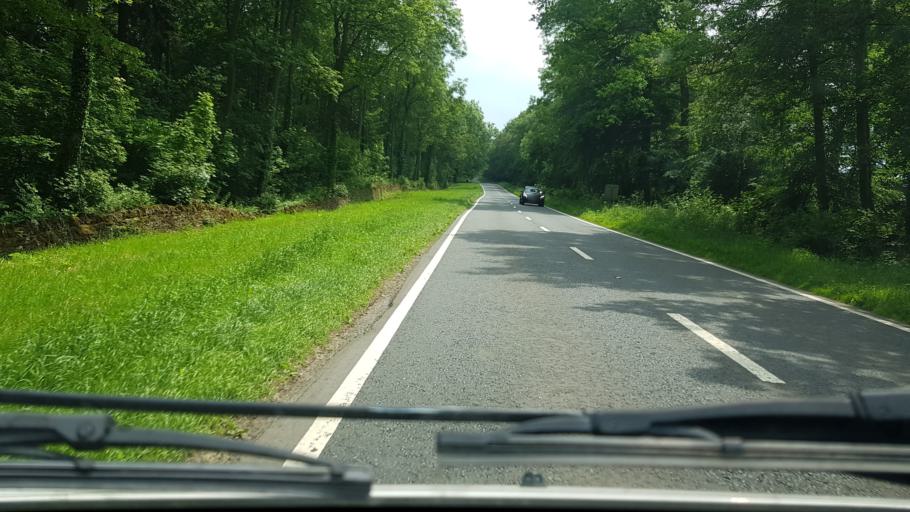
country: GB
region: England
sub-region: Gloucestershire
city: Chipping Campden
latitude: 52.0142
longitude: -1.7988
